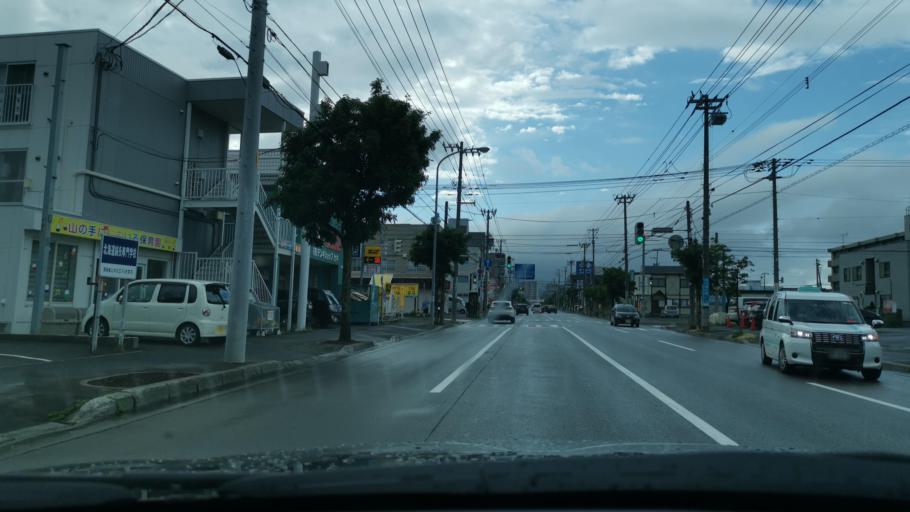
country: JP
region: Hokkaido
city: Sapporo
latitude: 43.0672
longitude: 141.2959
